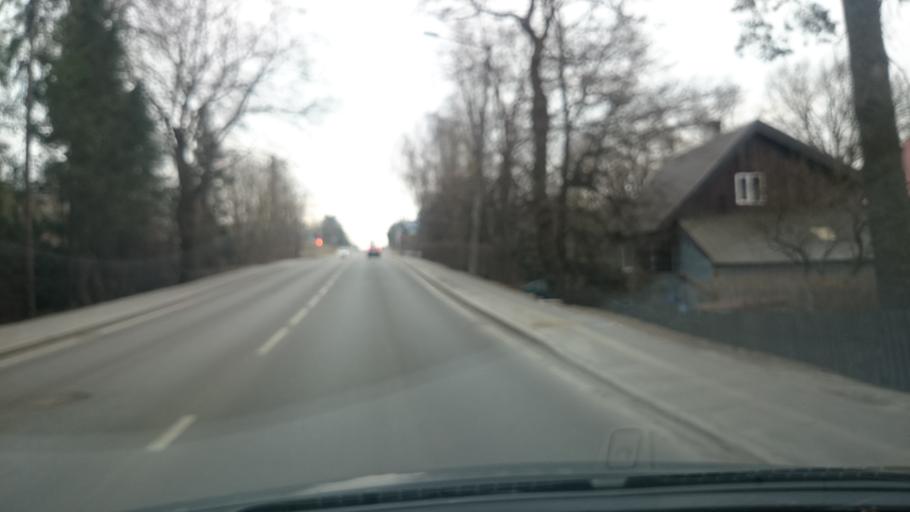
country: EE
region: Harju
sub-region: Saue vald
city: Laagri
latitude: 59.3882
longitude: 24.6410
